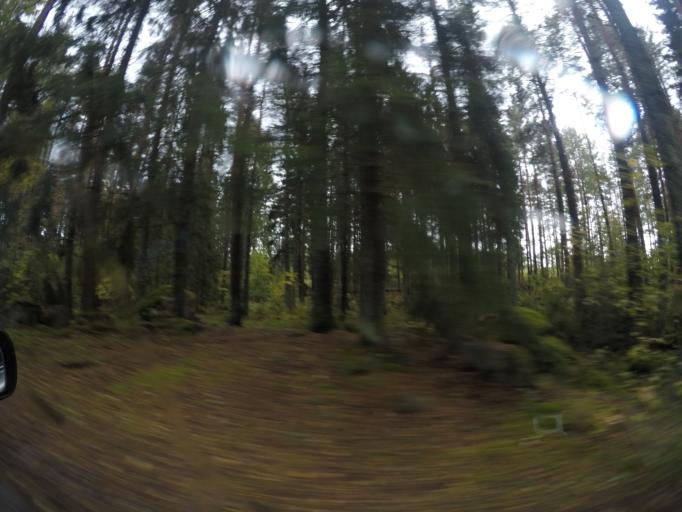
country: SE
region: Soedermanland
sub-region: Eskilstuna Kommun
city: Kvicksund
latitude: 59.3334
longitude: 16.2974
